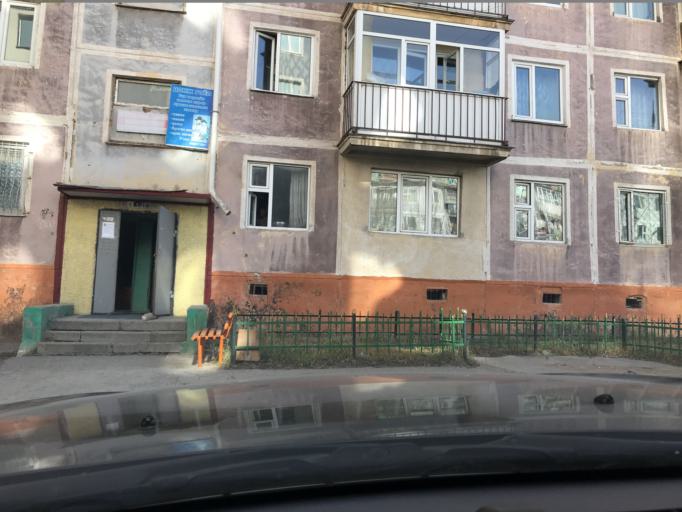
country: MN
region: Ulaanbaatar
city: Ulaanbaatar
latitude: 47.9192
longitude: 106.9476
